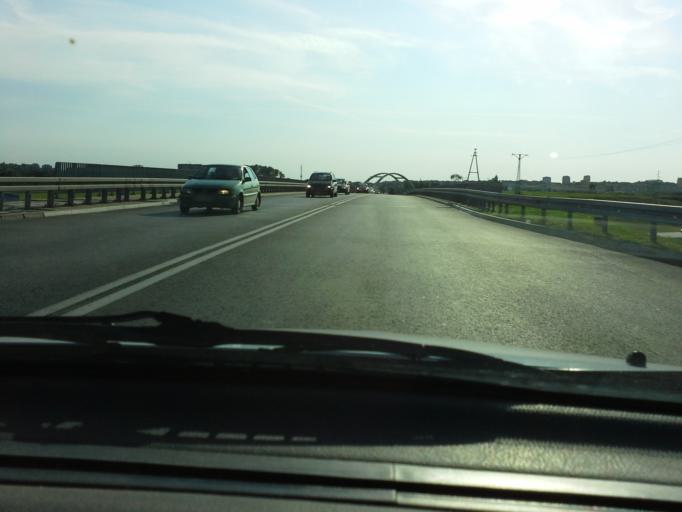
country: PL
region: Lesser Poland Voivodeship
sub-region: Powiat chrzanowski
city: Chrzanow
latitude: 50.1481
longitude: 19.4296
